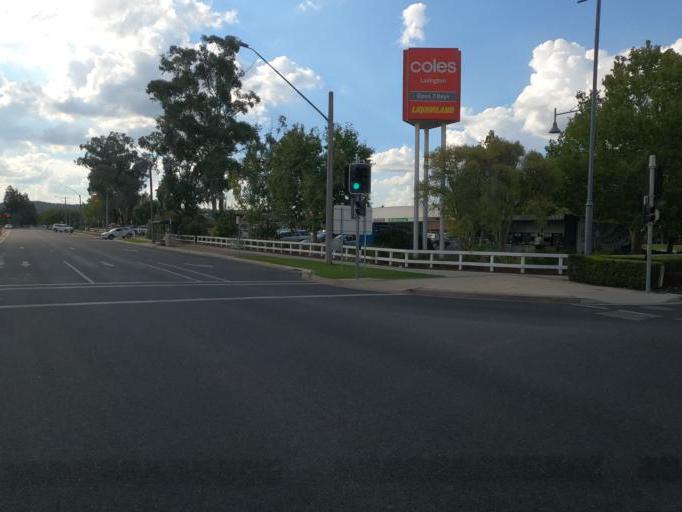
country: AU
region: New South Wales
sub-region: Albury Municipality
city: Lavington
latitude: -36.0510
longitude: 146.9326
